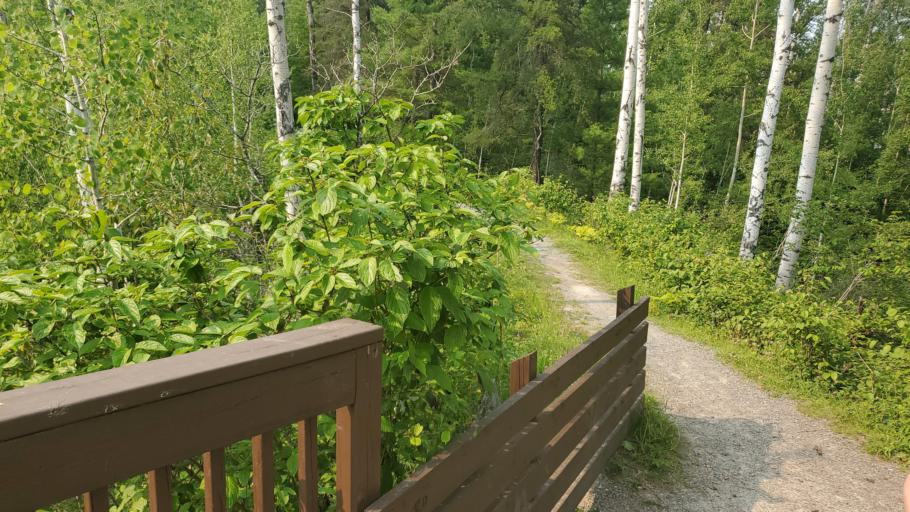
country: CA
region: Ontario
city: Englehart
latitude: 47.7973
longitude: -79.8869
